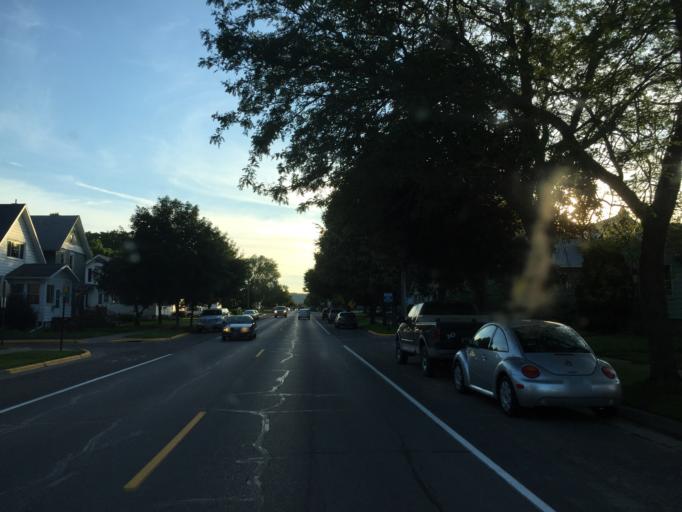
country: US
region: Minnesota
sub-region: Winona County
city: Winona
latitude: 44.0541
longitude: -91.6564
